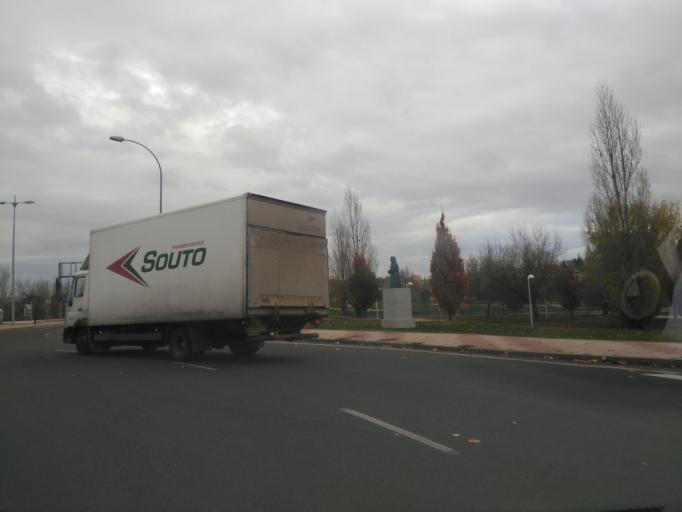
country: ES
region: Castille and Leon
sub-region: Provincia de Salamanca
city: Salamanca
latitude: 40.9577
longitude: -5.6755
